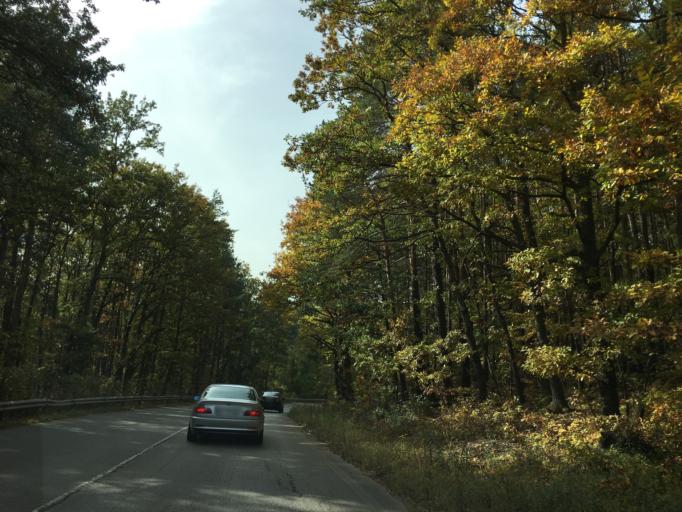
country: BG
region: Sofiya
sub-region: Obshtina Samokov
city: Samokov
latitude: 42.5069
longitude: 23.5330
